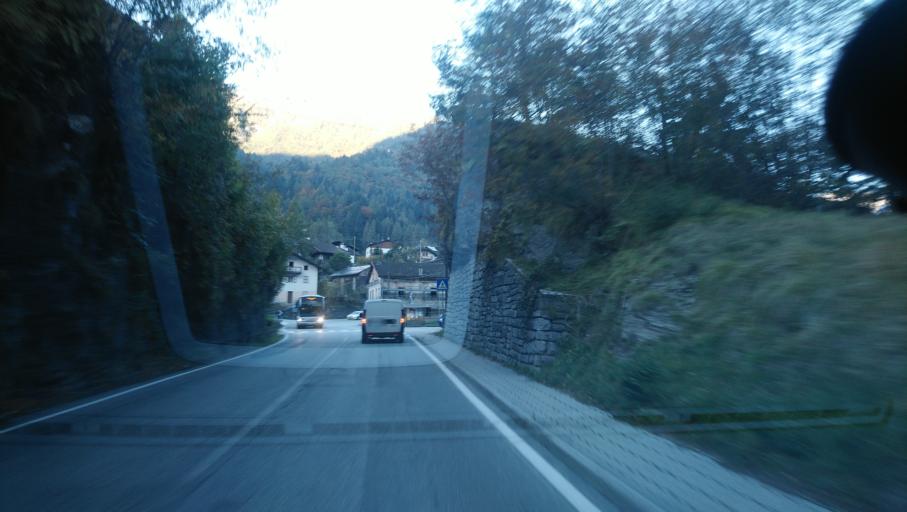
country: IT
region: Veneto
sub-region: Provincia di Belluno
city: Cencenighe Agordino
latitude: 46.3434
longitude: 11.9743
